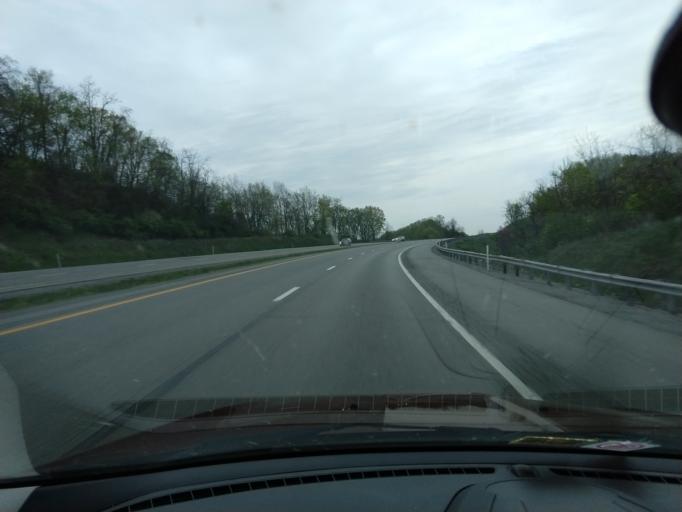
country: US
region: West Virginia
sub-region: Lewis County
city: Weston
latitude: 38.9338
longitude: -80.5438
